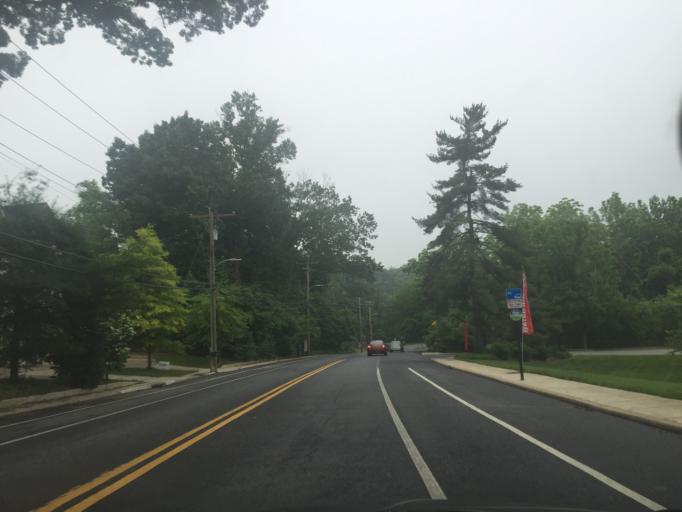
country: US
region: Maryland
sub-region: Baltimore County
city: Pikesville
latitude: 39.3660
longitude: -76.6752
